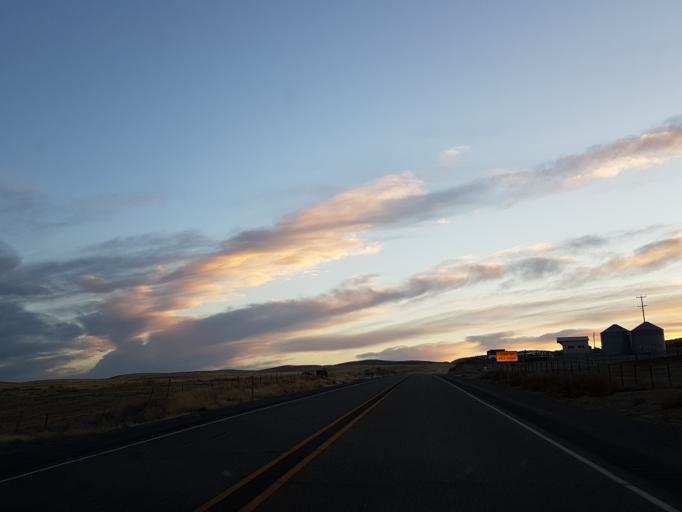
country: US
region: Oregon
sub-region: Malheur County
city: Vale
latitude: 43.9263
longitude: -117.3984
